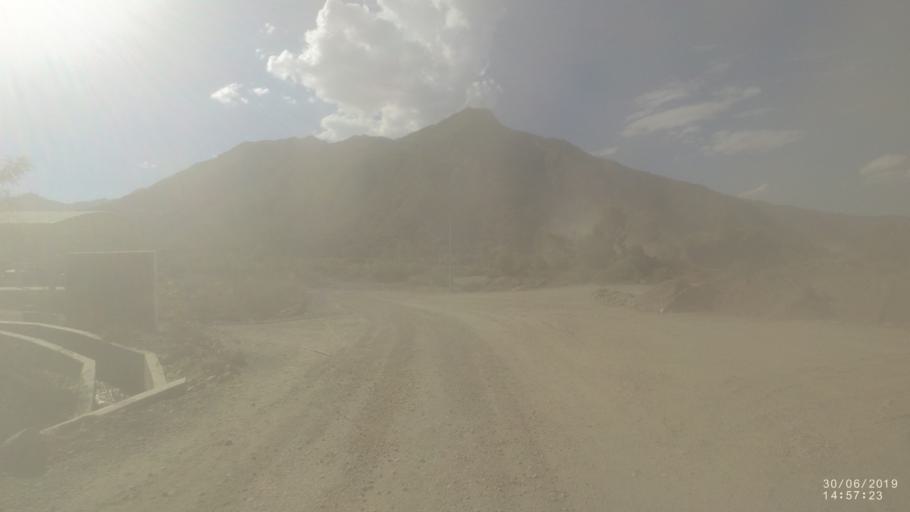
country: BO
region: Cochabamba
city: Irpa Irpa
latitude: -17.7440
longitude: -66.3533
